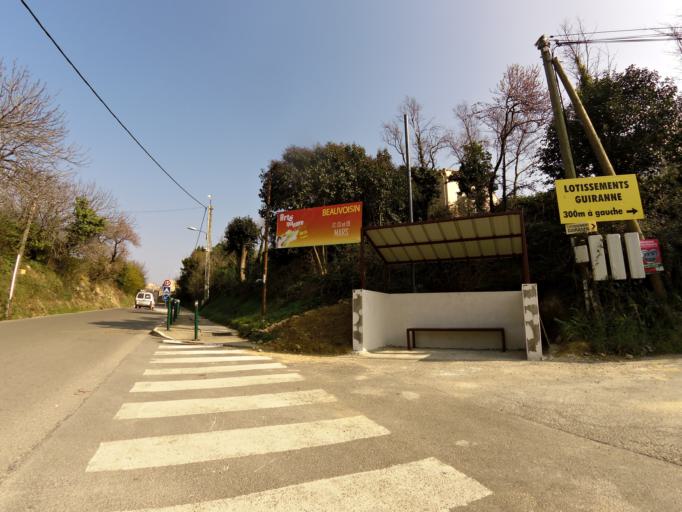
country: FR
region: Languedoc-Roussillon
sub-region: Departement du Gard
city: Beauvoisin
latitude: 43.7176
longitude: 4.3160
